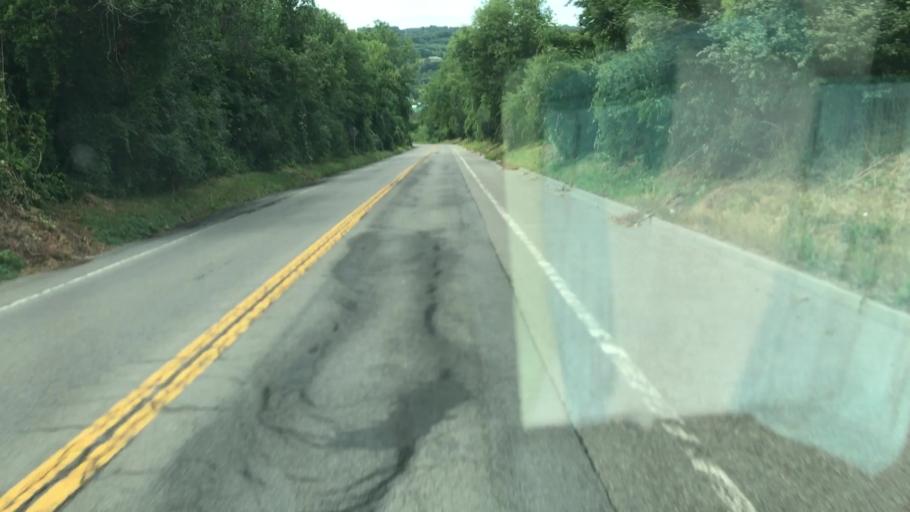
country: US
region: New York
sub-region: Onondaga County
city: Marcellus
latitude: 42.9328
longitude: -76.3199
